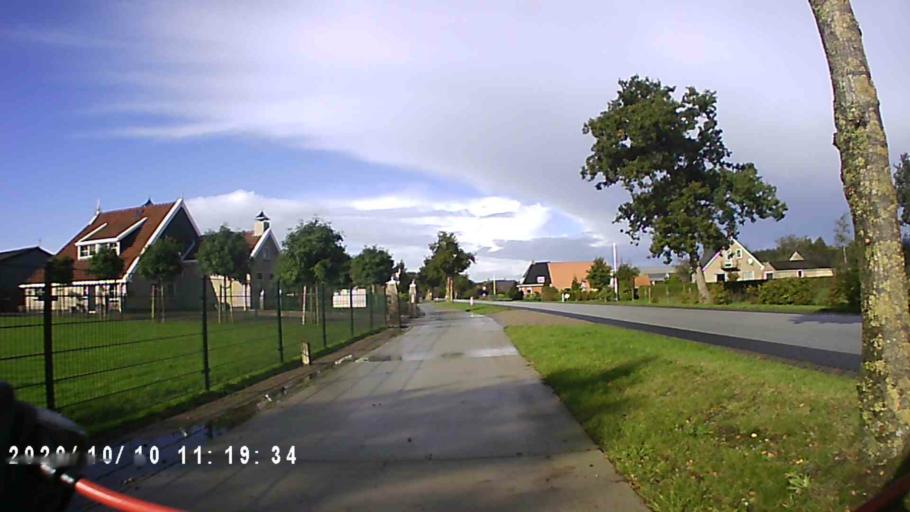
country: NL
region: Friesland
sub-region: Gemeente Smallingerland
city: Drachtstercompagnie
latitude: 53.0949
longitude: 6.1909
